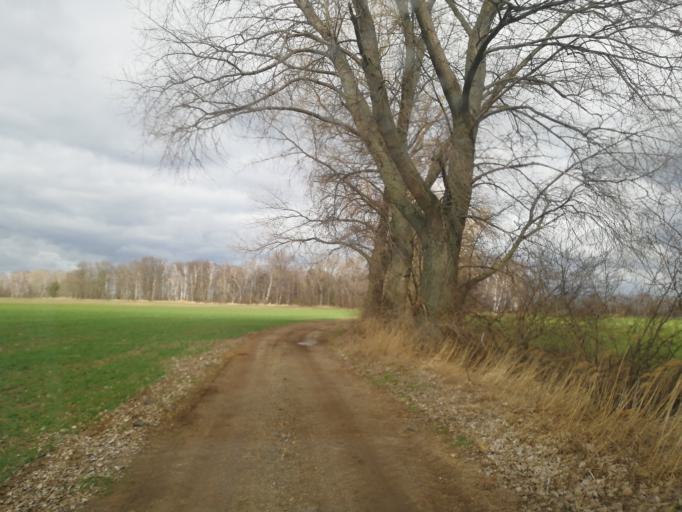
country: DE
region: Brandenburg
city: Schonewalde
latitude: 51.6697
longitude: 13.5612
